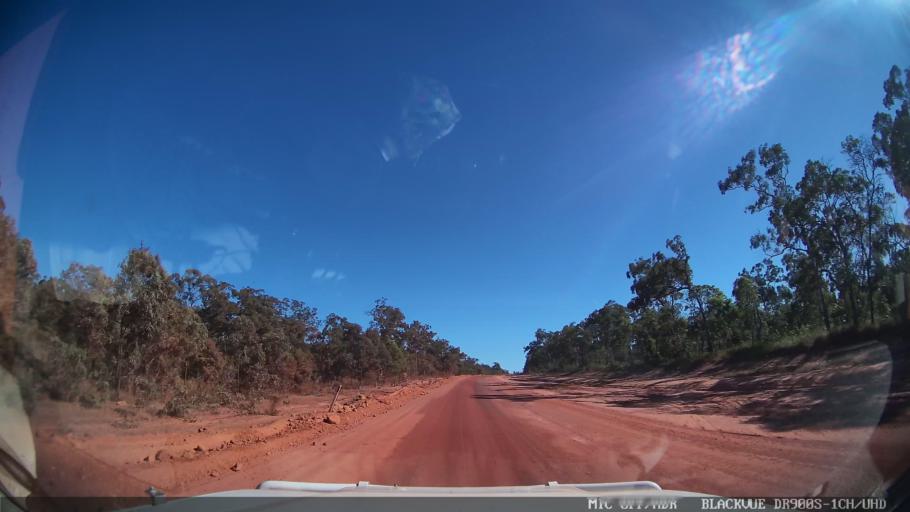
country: AU
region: Queensland
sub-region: Torres
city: Thursday Island
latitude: -11.4001
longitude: 142.3579
